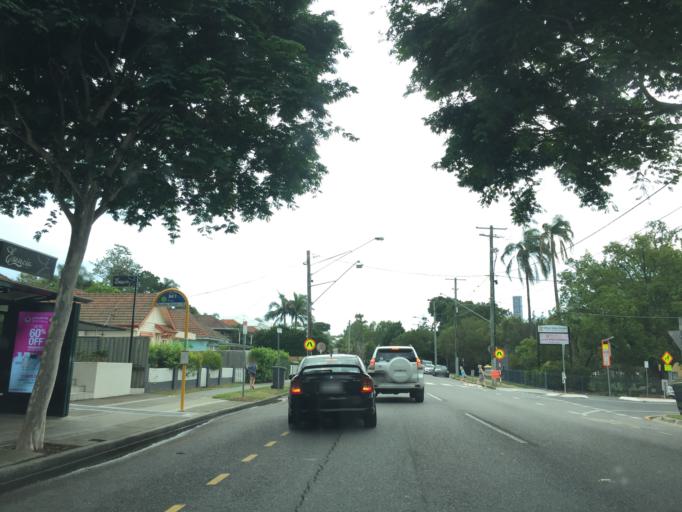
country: AU
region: Queensland
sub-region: Brisbane
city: Milton
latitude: -27.4662
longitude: 152.9976
